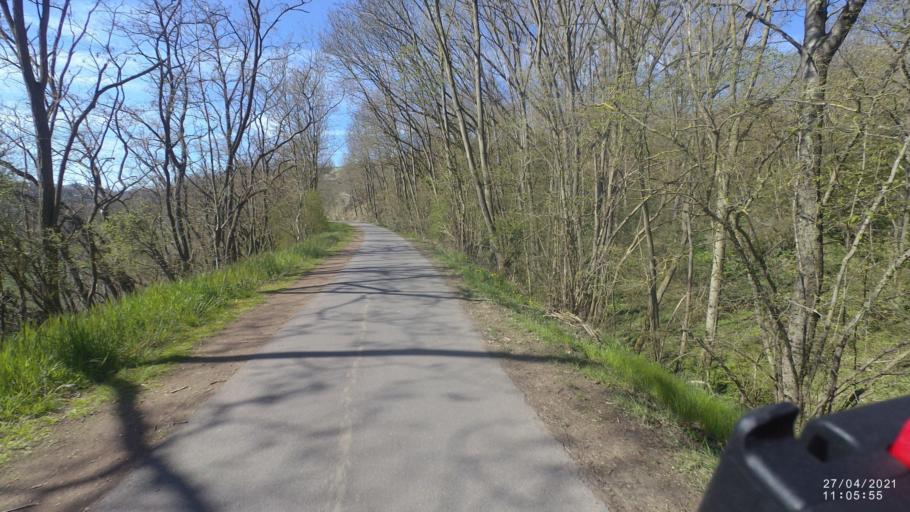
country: DE
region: Rheinland-Pfalz
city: Trimbs
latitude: 50.3216
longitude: 7.2725
